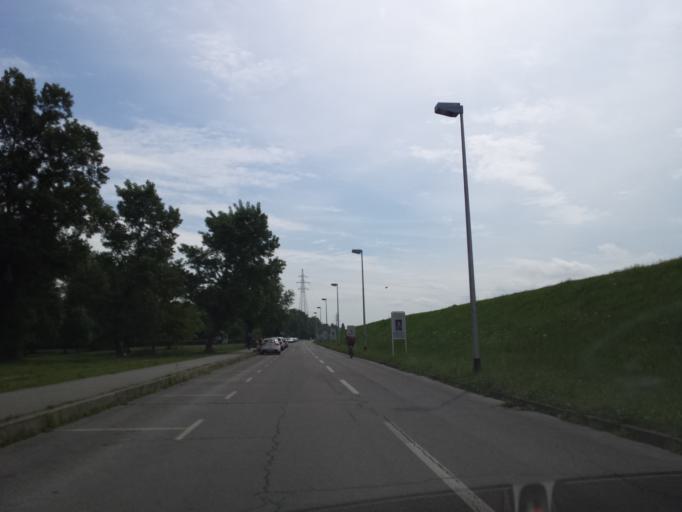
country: HR
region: Grad Zagreb
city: Jankomir
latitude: 45.7780
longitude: 15.9142
